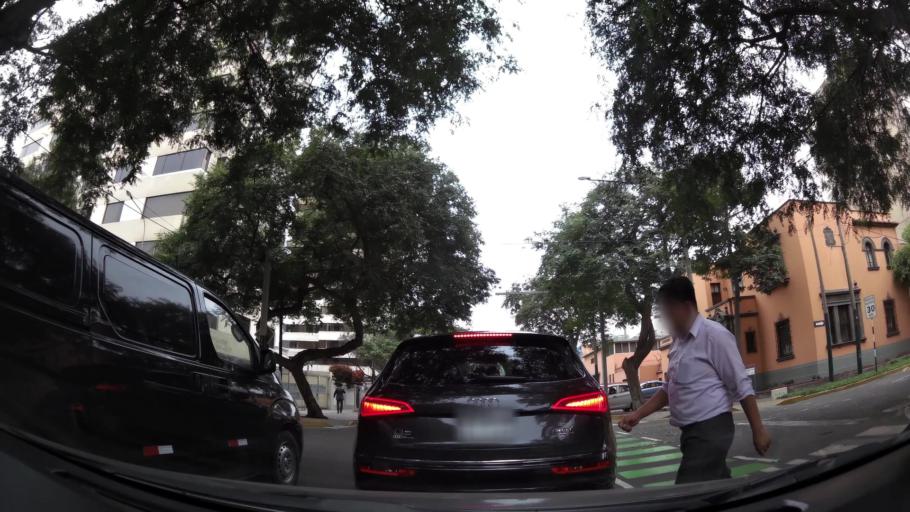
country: PE
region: Lima
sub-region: Lima
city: San Isidro
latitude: -12.0910
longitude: -77.0357
